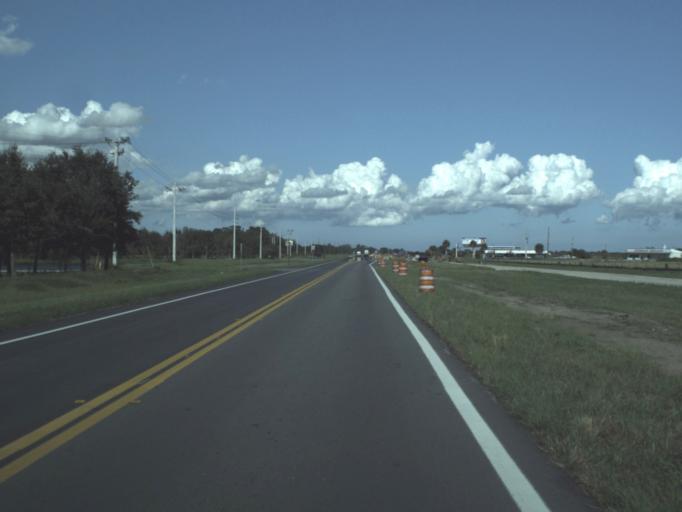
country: US
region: Florida
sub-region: Okeechobee County
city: Taylor Creek
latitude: 27.2890
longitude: -80.7010
